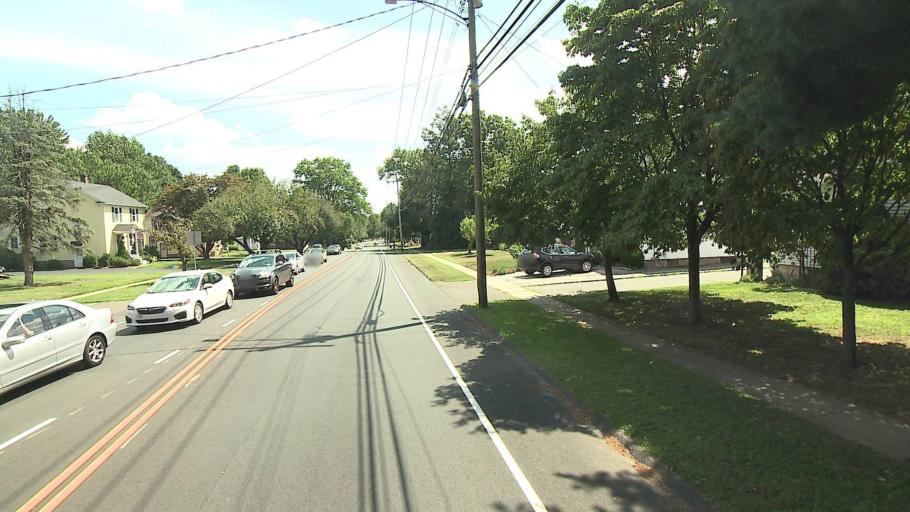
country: US
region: Connecticut
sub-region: Fairfield County
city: Stratford
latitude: 41.2190
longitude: -73.1482
